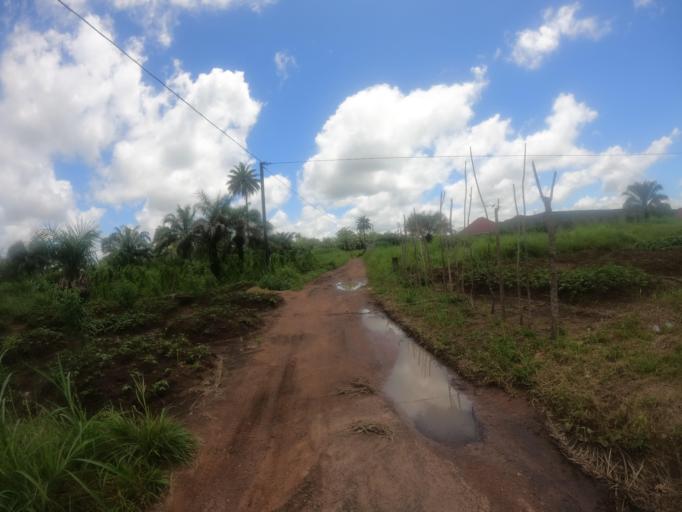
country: SL
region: Northern Province
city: Makeni
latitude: 8.8744
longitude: -12.0949
